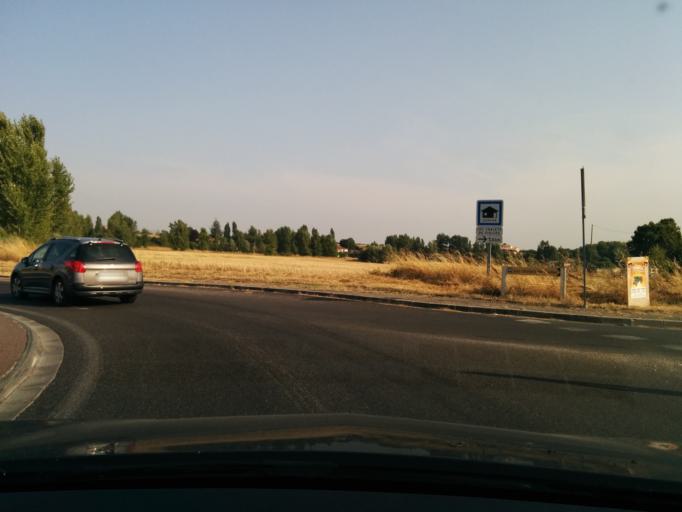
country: FR
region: Midi-Pyrenees
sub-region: Departement du Tarn
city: Brens
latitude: 43.8828
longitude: 1.8985
